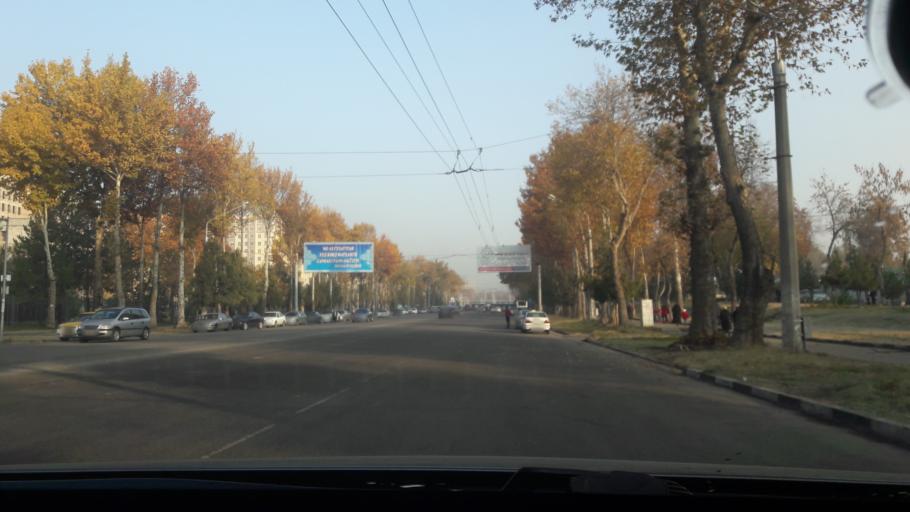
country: TJ
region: Dushanbe
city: Dushanbe
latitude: 38.5780
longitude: 68.7551
